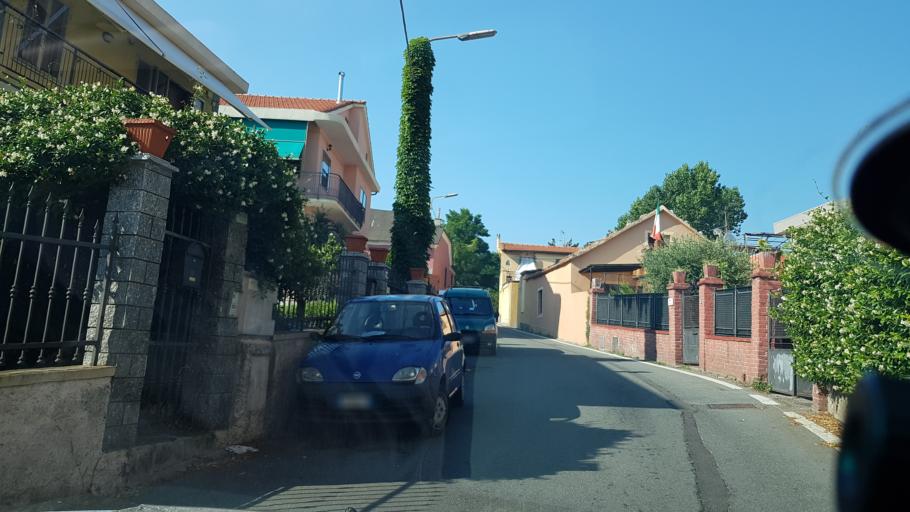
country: IT
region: Liguria
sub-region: Provincia di Genova
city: Genoa
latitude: 44.4462
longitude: 8.9005
